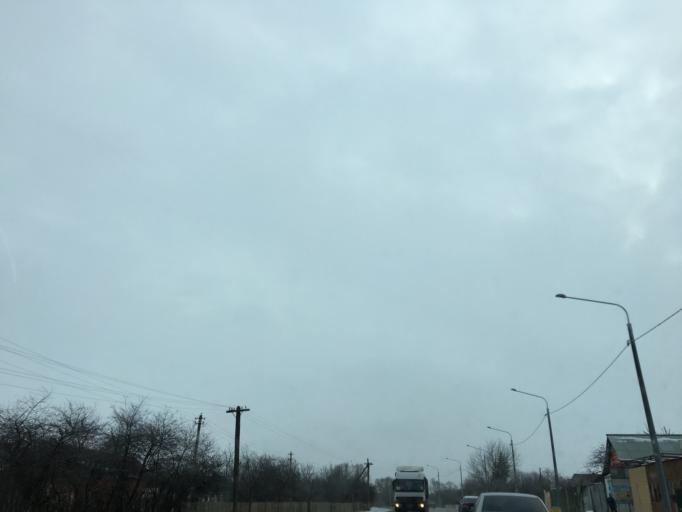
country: RU
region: Tula
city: Borodinskiy
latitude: 54.0262
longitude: 37.8899
